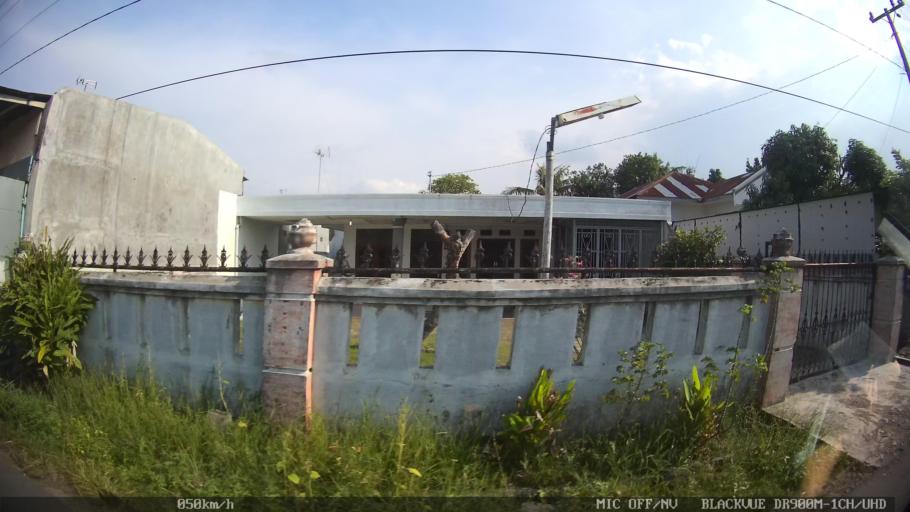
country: ID
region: North Sumatra
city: Medan
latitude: 3.5940
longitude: 98.7592
